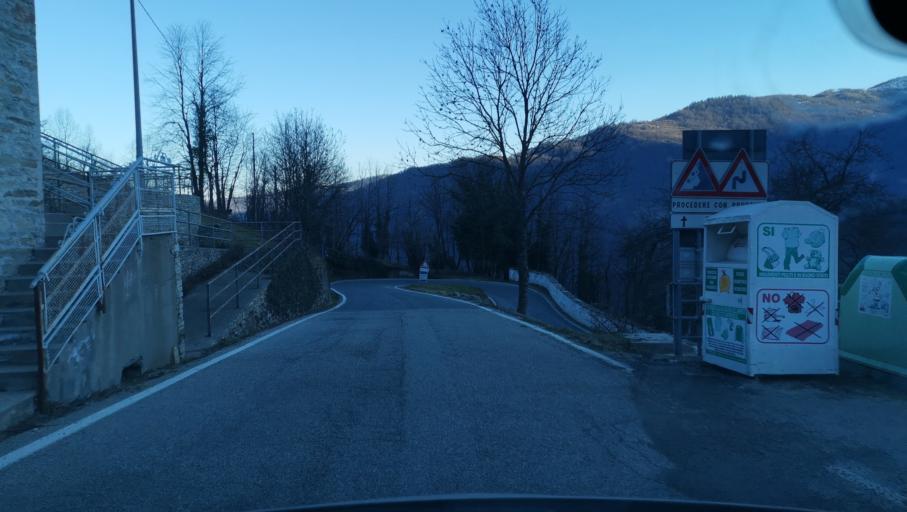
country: IT
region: Piedmont
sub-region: Provincia di Torino
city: Rora
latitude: 44.7919
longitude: 7.2001
